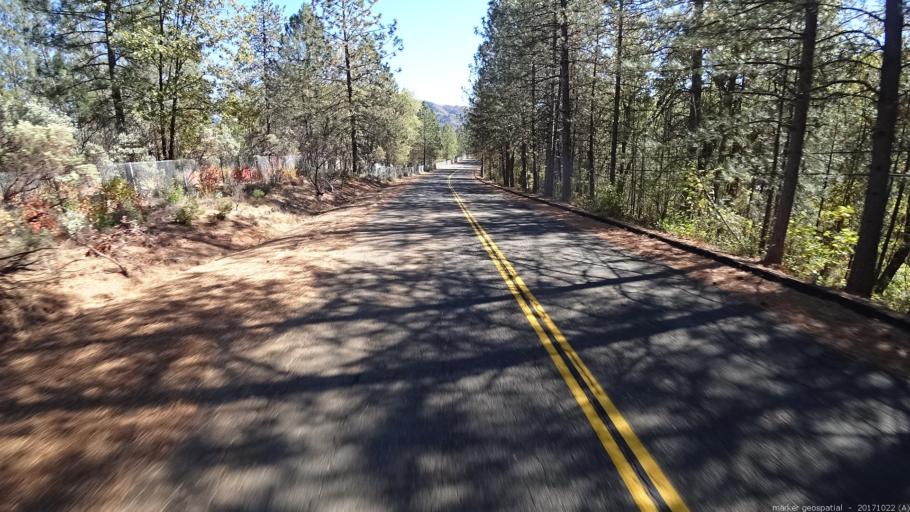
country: US
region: California
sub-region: Shasta County
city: Central Valley (historical)
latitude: 40.9163
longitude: -122.3967
